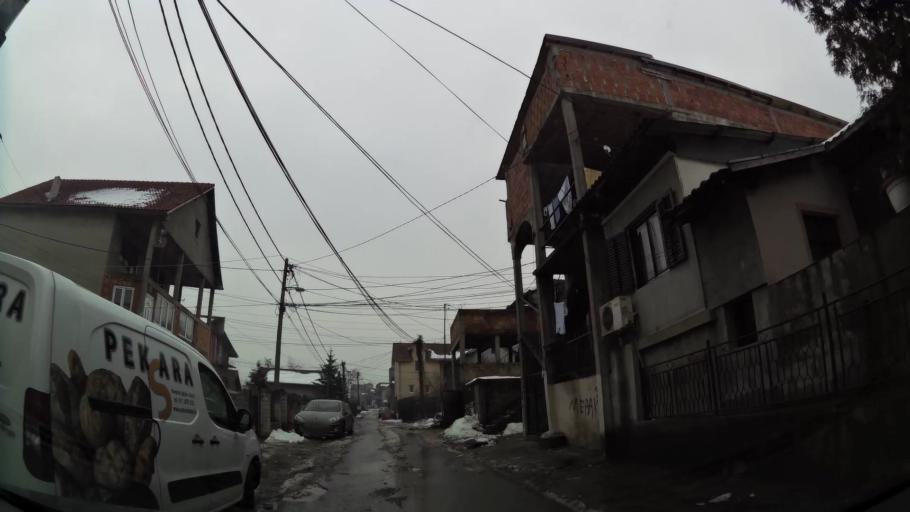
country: RS
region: Central Serbia
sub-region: Belgrade
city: Zvezdara
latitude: 44.7758
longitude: 20.5078
